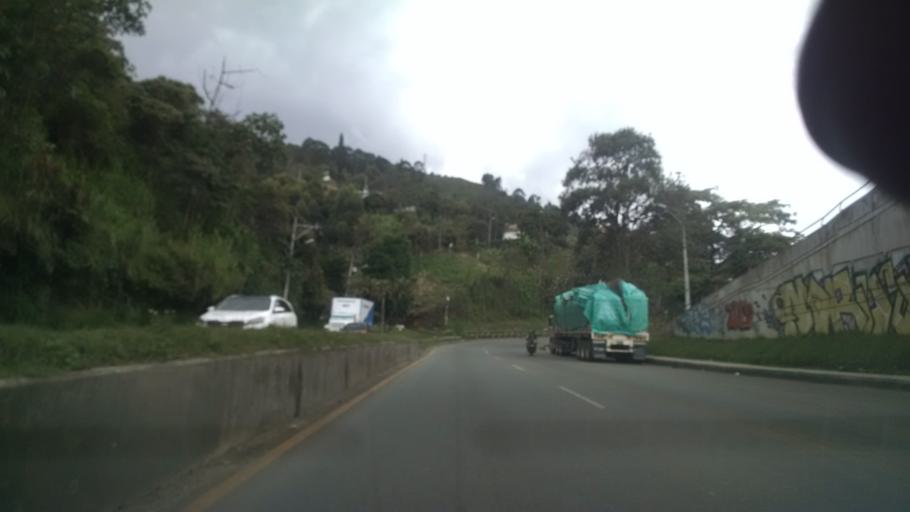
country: CO
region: Antioquia
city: Sabaneta
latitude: 6.1387
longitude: -75.6319
